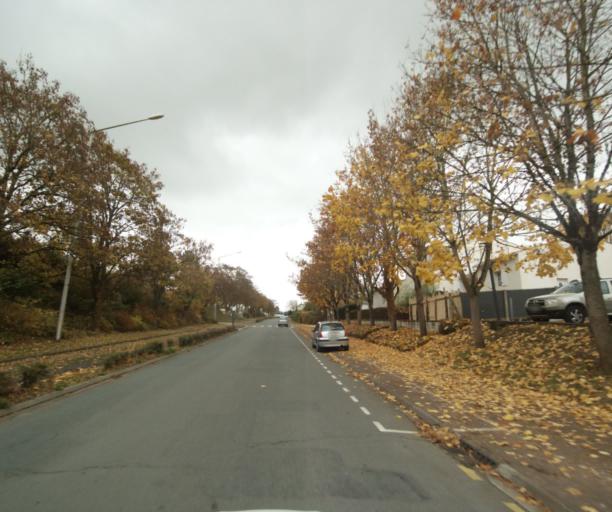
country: FR
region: Poitou-Charentes
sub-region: Departement de la Charente-Maritime
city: Saintes
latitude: 45.7382
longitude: -0.6536
